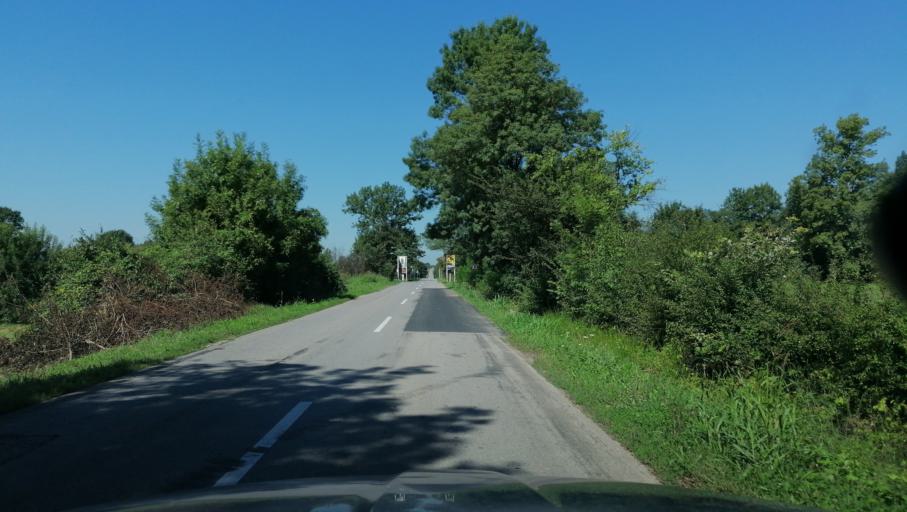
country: RS
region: Central Serbia
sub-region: Raski Okrug
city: Vrnjacka Banja
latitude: 43.6828
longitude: 20.8887
